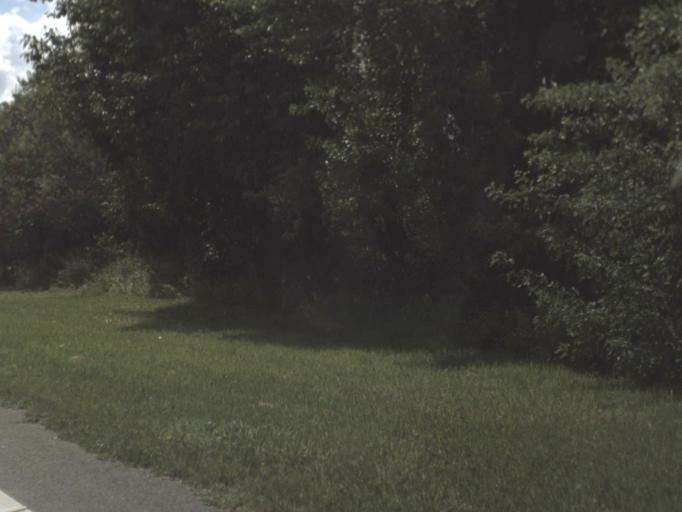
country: US
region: Florida
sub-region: Collier County
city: Immokalee
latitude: 26.2647
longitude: -81.3421
